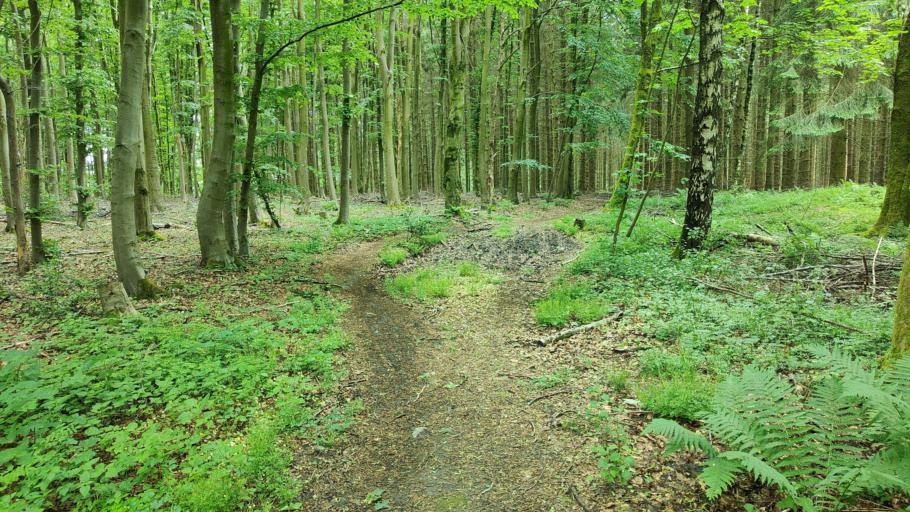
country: BE
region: Wallonia
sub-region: Province de Liege
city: La Calamine
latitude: 50.7296
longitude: 6.0599
